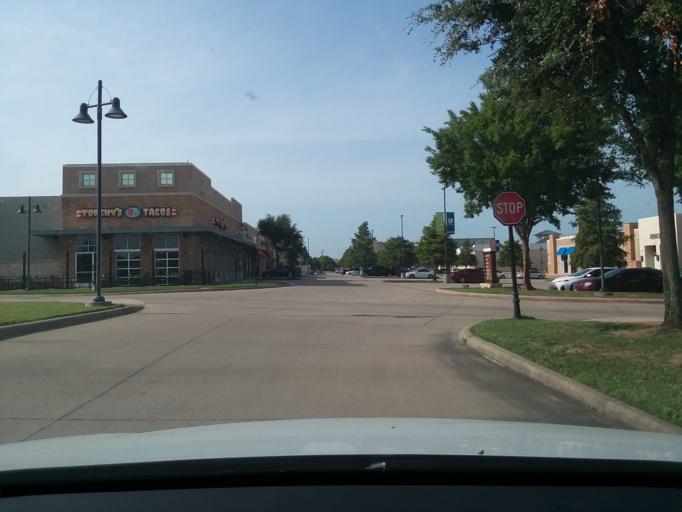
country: US
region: Texas
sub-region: Denton County
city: Copper Canyon
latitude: 33.0750
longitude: -97.0842
